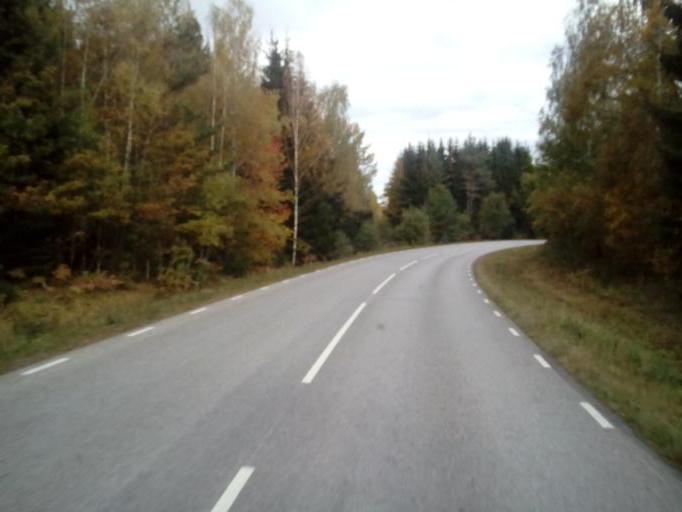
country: SE
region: Kalmar
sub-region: Vasterviks Kommun
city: Gamleby
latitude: 57.8847
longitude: 16.3196
